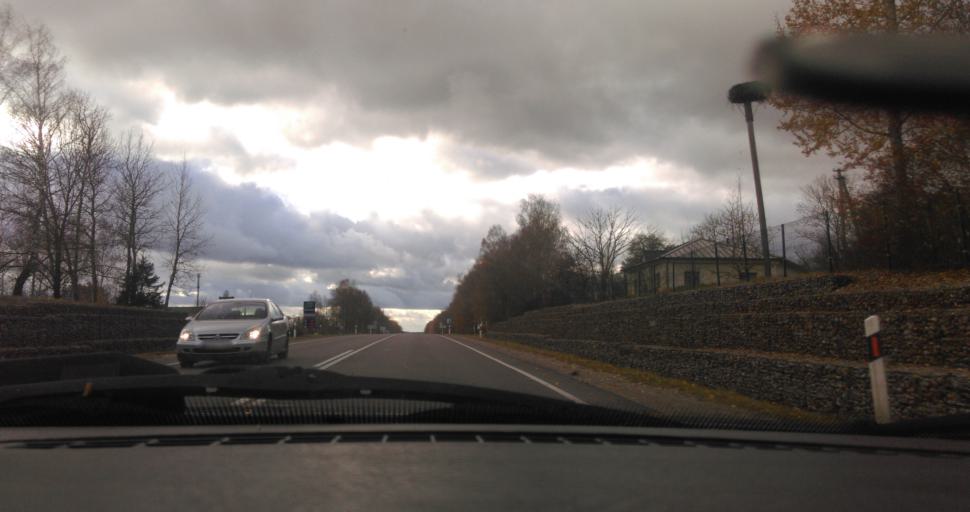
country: LT
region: Utenos apskritis
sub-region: Utena
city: Utena
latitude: 55.5138
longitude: 25.6464
